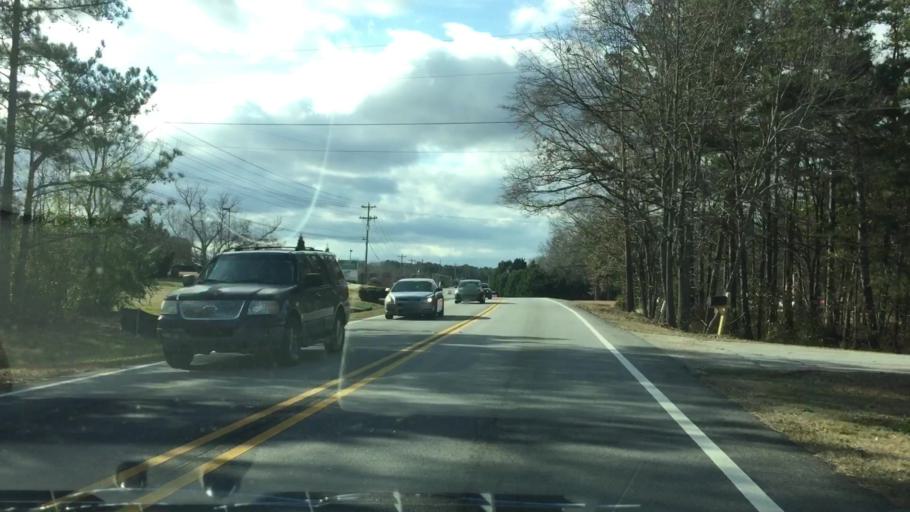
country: US
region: Georgia
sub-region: Henry County
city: McDonough
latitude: 33.4289
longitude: -84.0932
